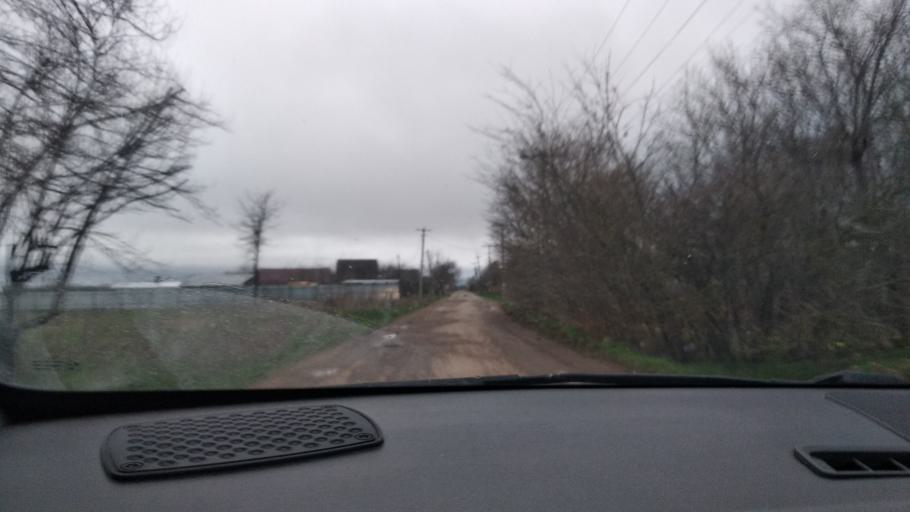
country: RU
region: Krasnodarskiy
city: Afipskiy
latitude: 44.8951
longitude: 38.7620
